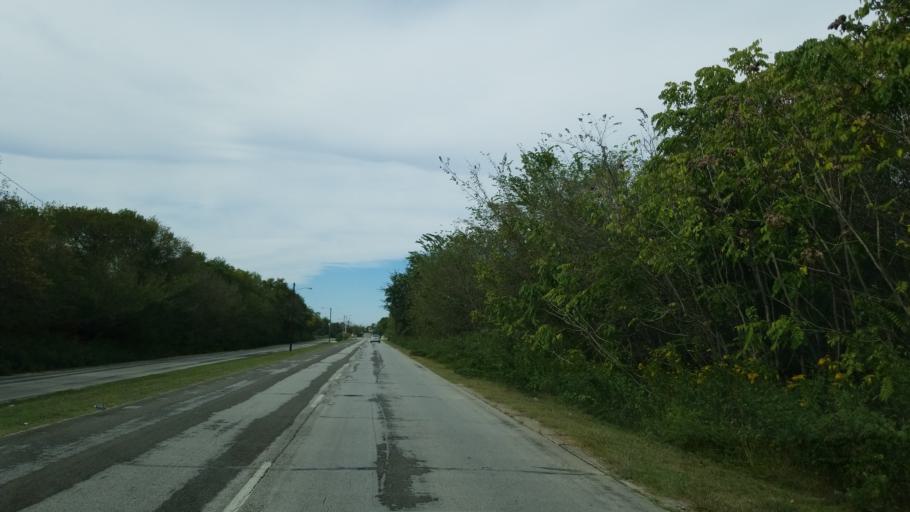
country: US
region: Texas
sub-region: Dallas County
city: Dallas
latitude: 32.7536
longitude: -96.7357
